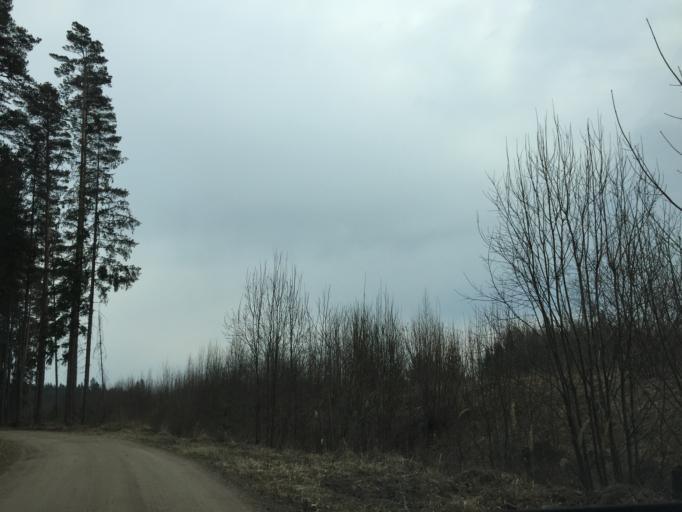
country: LV
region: Amatas Novads
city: Drabesi
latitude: 57.2075
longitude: 25.2378
